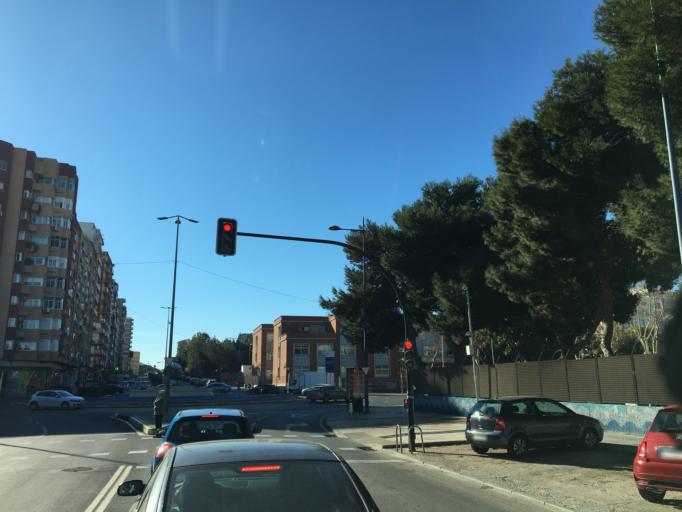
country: ES
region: Murcia
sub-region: Murcia
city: Cartagena
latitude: 37.6076
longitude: -0.9779
